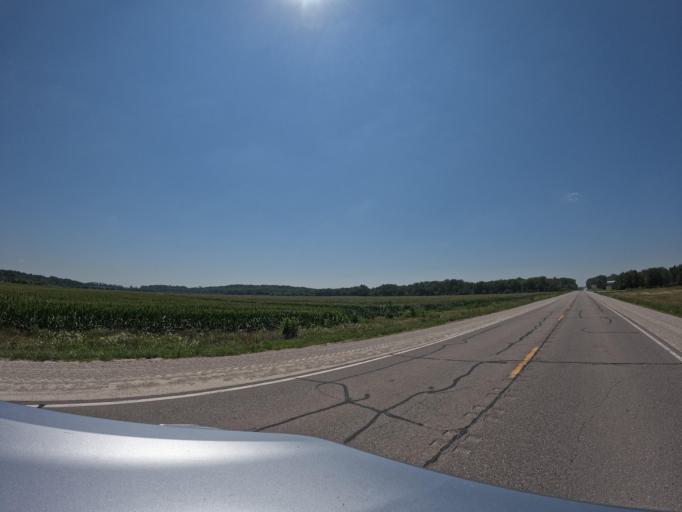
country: US
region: Iowa
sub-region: Keokuk County
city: Sigourney
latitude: 41.3138
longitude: -92.2051
